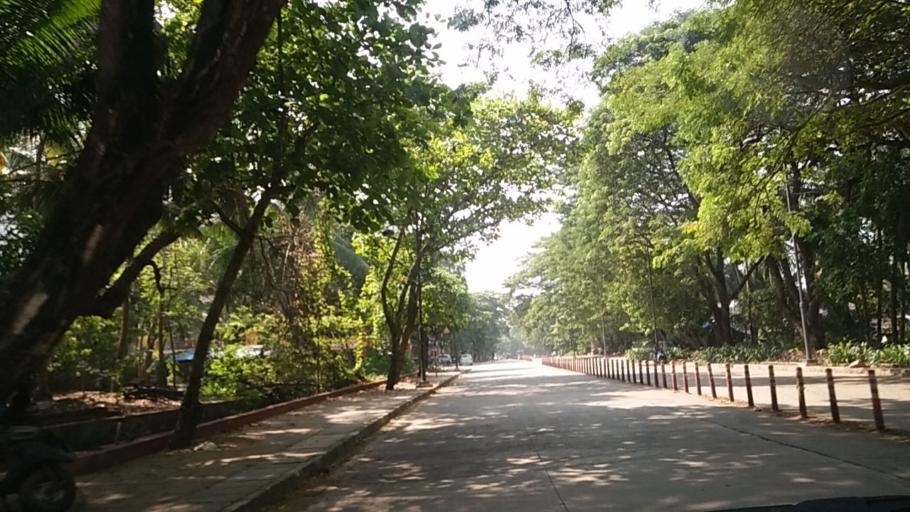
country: IN
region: Goa
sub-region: North Goa
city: Taleigao
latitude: 15.4684
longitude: 73.8073
